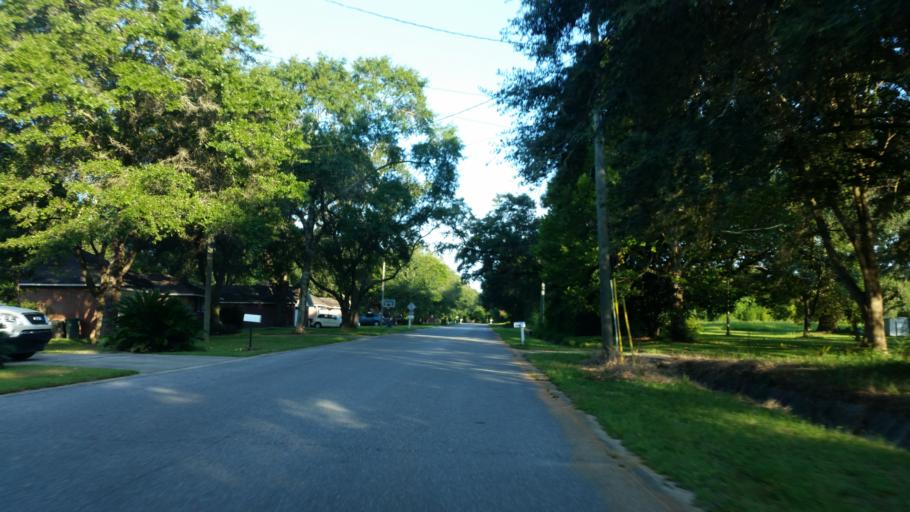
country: US
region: Florida
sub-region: Escambia County
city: Bellview
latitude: 30.4854
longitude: -87.3338
